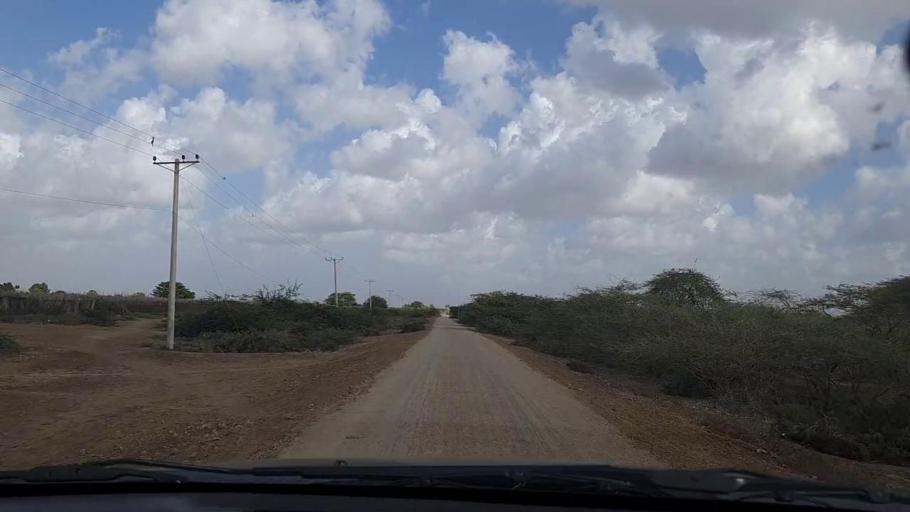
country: PK
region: Sindh
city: Keti Bandar
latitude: 24.0990
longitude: 67.6010
